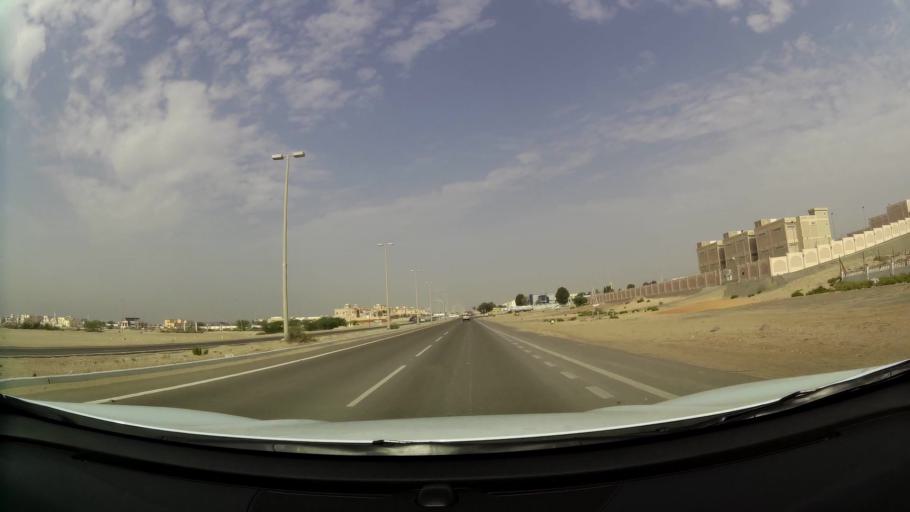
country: AE
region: Abu Dhabi
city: Abu Dhabi
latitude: 24.2910
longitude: 54.6600
